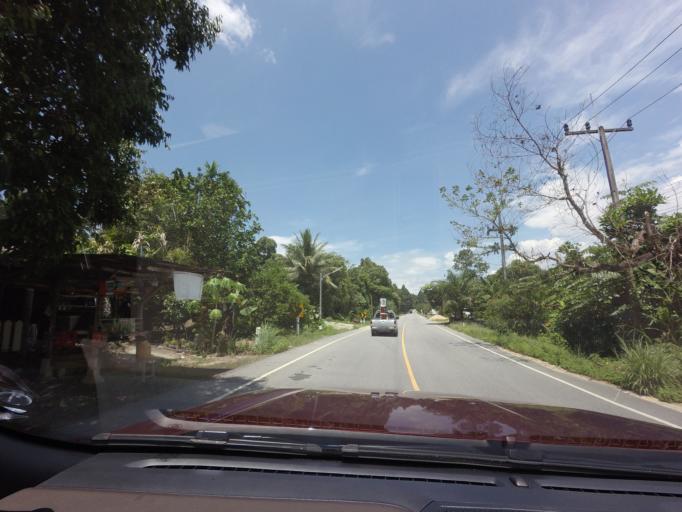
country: TH
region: Narathiwat
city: Chanae
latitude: 6.1413
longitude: 101.7019
